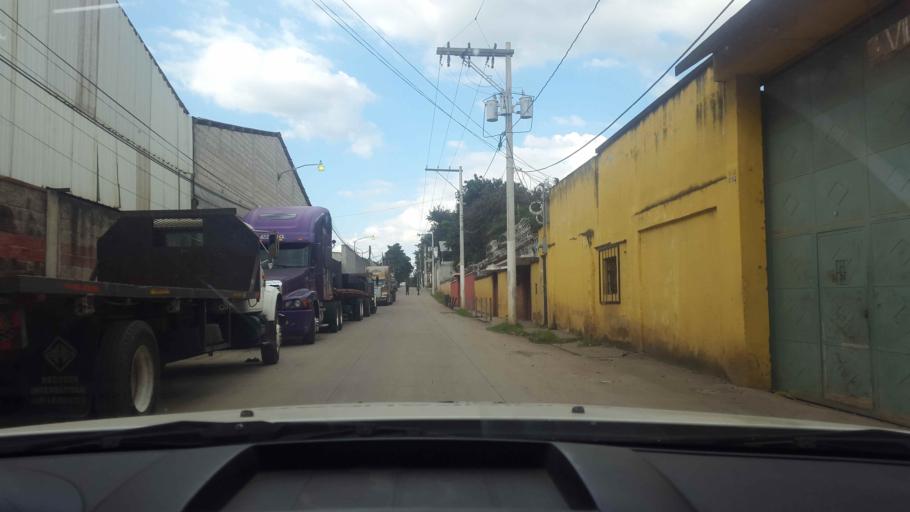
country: GT
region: Guatemala
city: Petapa
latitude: 14.5097
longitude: -90.5387
